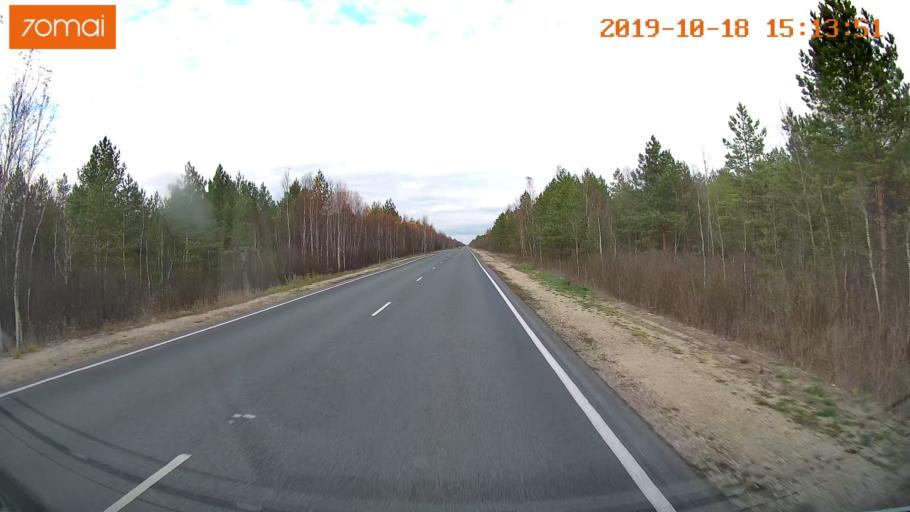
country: RU
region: Vladimir
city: Gus'-Khrustal'nyy
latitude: 55.5933
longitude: 40.7190
